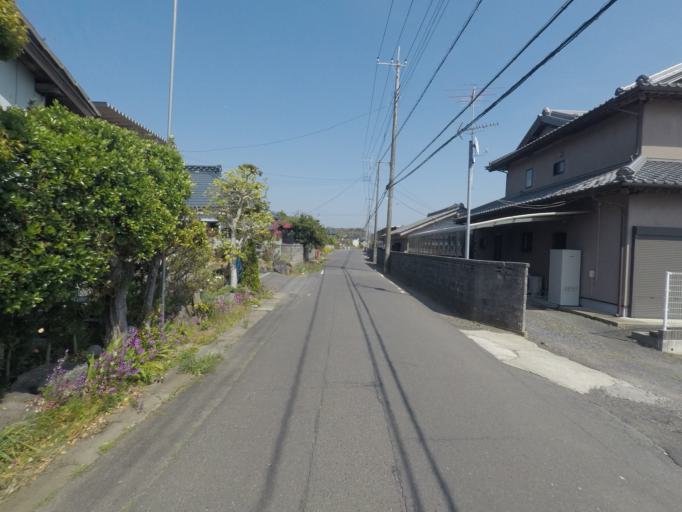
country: JP
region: Ibaraki
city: Inashiki
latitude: 36.0707
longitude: 140.3129
